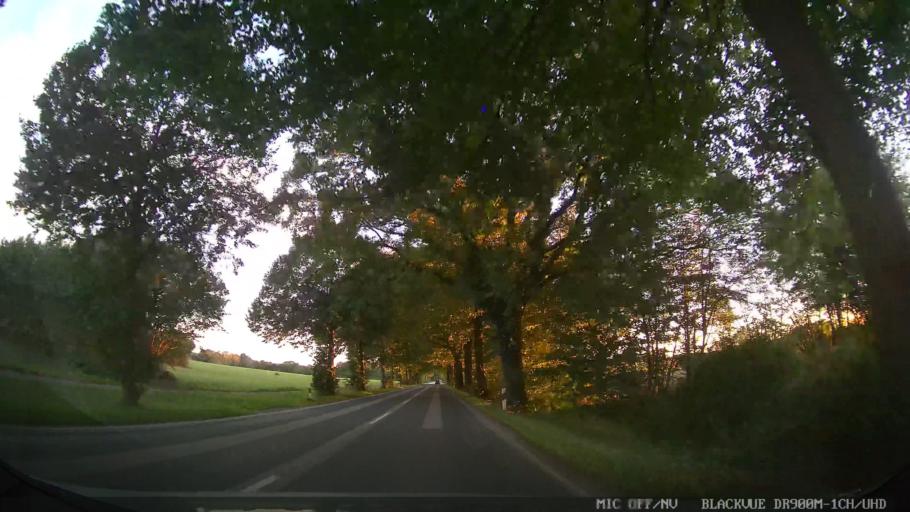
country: DE
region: Schleswig-Holstein
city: Susel
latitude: 54.0655
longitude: 10.6873
